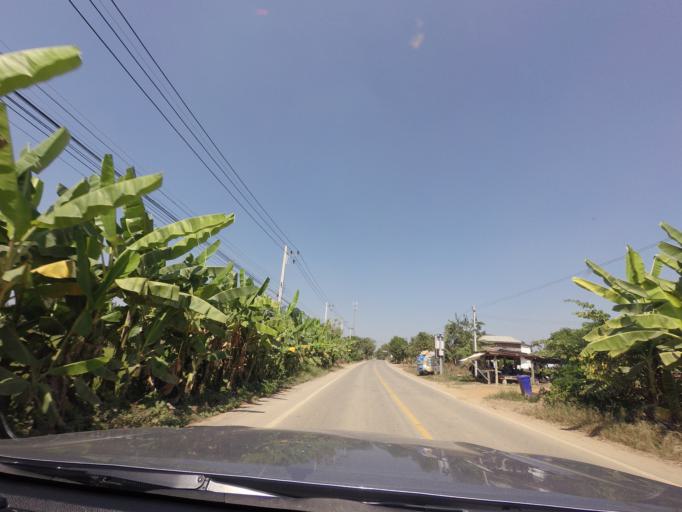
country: TH
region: Sukhothai
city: Sawankhalok
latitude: 17.2346
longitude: 99.7751
